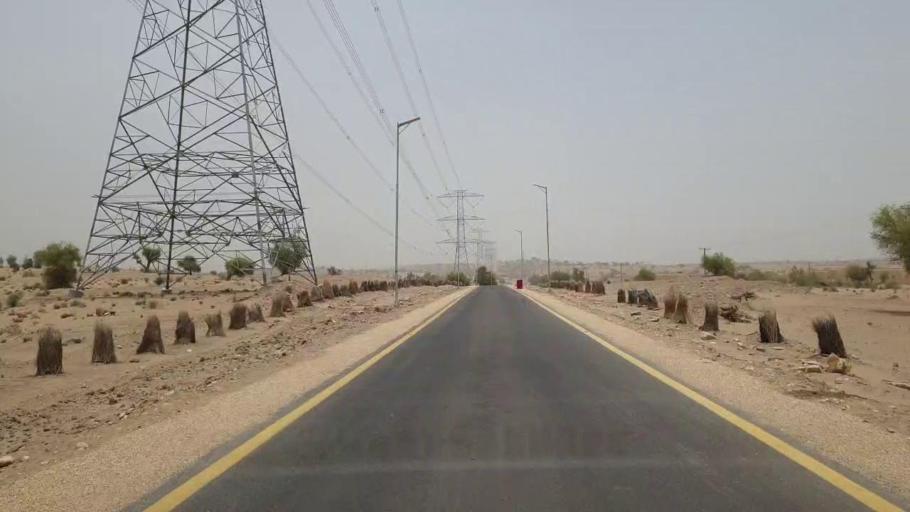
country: PK
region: Sindh
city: Islamkot
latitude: 24.7272
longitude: 70.3156
